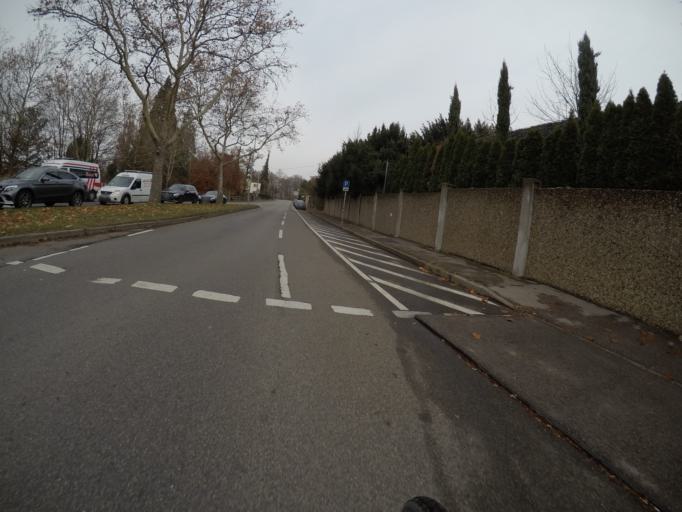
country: DE
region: Baden-Wuerttemberg
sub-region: Regierungsbezirk Stuttgart
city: Stuttgart
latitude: 48.7474
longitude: 9.1569
